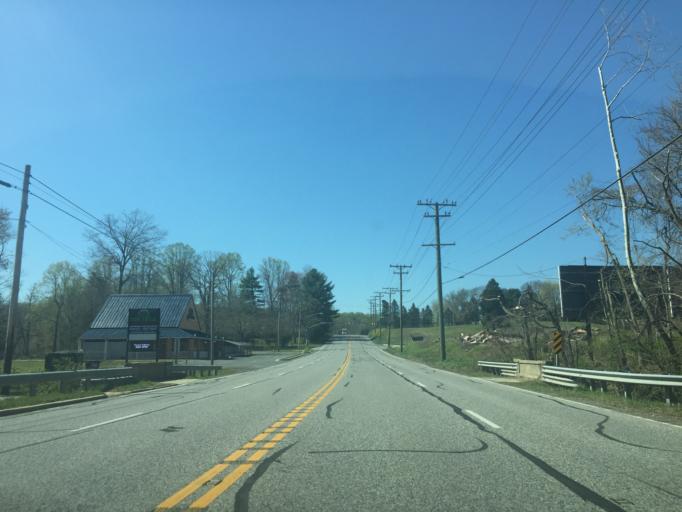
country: US
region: Maryland
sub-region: Harford County
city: Pleasant Hills
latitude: 39.4836
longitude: -76.4022
